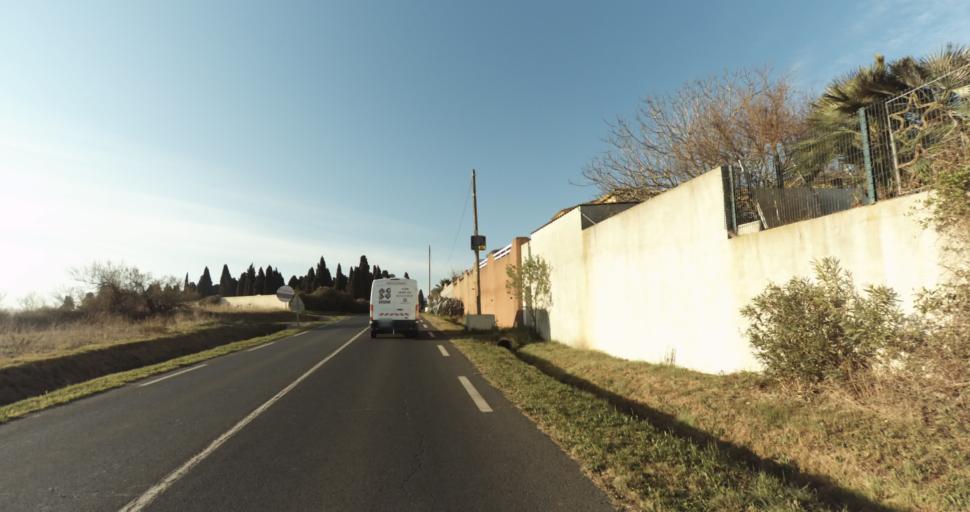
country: FR
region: Languedoc-Roussillon
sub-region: Departement de l'Herault
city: Marseillan
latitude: 43.3618
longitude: 3.5306
